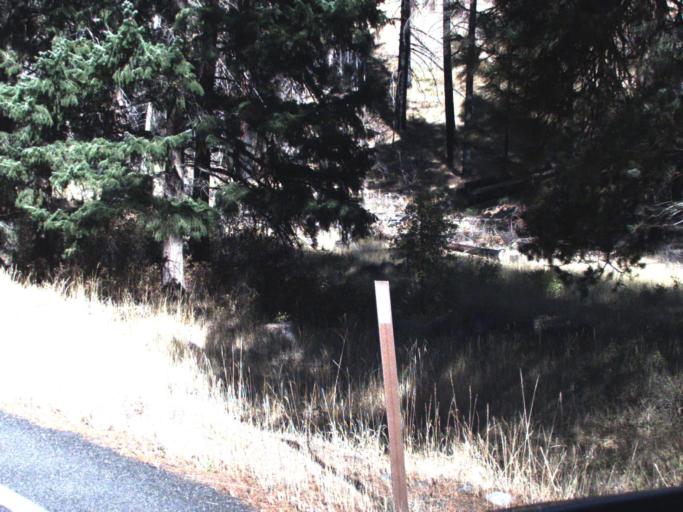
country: US
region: Washington
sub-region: Yakima County
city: Tieton
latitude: 46.6741
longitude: -121.0435
